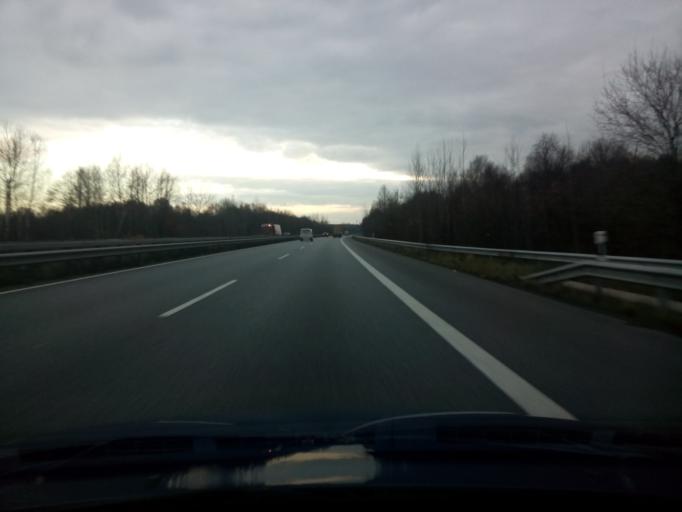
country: DE
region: Lower Saxony
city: Uthlede
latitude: 53.3223
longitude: 8.6198
